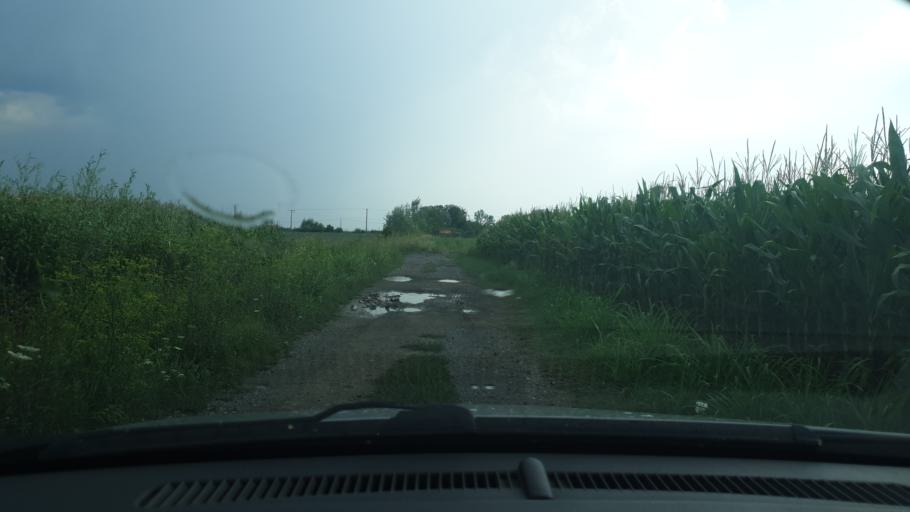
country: RS
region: Autonomna Pokrajina Vojvodina
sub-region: Sremski Okrug
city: Sremska Mitrovica
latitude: 44.9543
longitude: 19.6177
